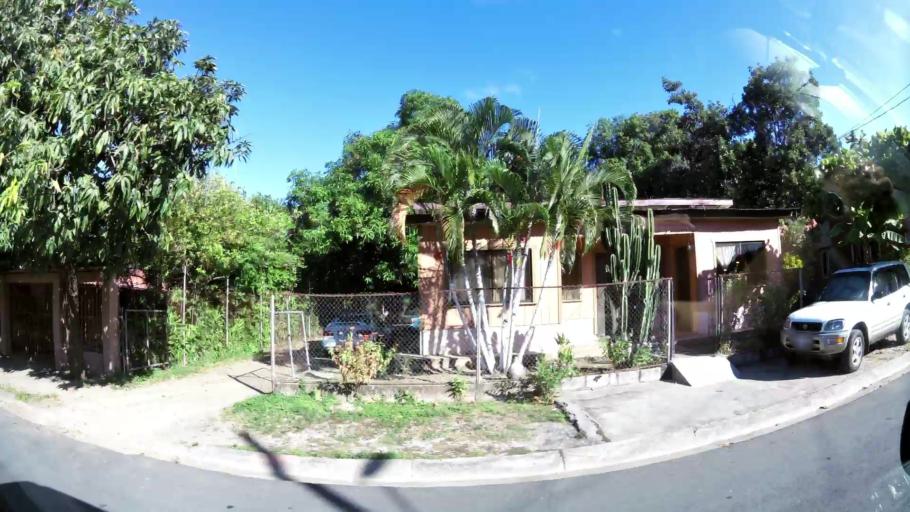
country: CR
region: Guanacaste
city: Belen
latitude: 10.4467
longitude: -85.5498
